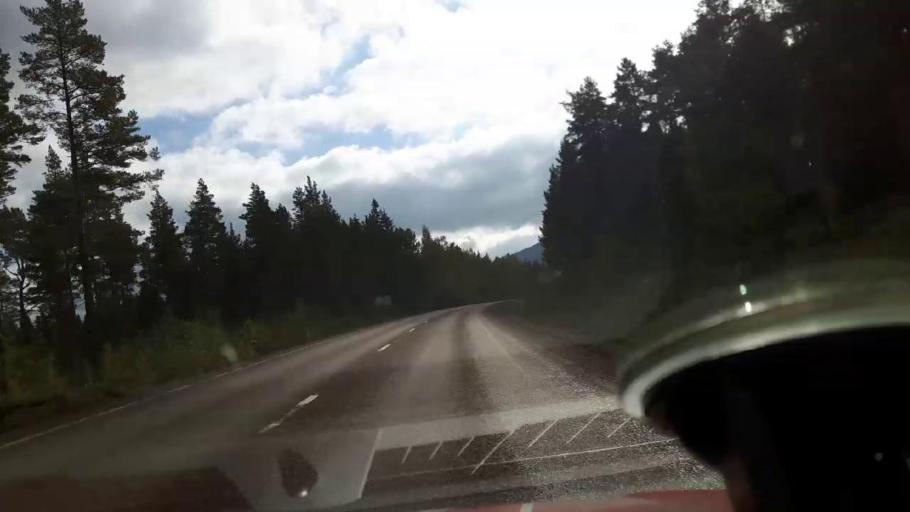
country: SE
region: Gaevleborg
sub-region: Bollnas Kommun
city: Arbra
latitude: 61.5852
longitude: 16.3140
